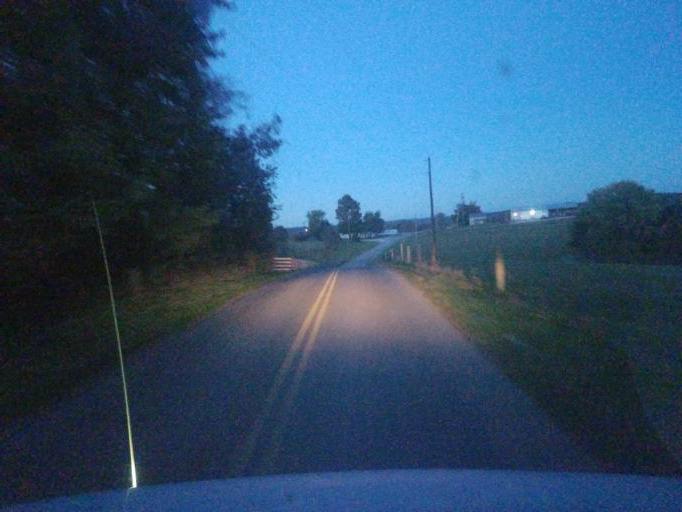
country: US
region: Ohio
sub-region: Perry County
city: Somerset
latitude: 39.8726
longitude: -82.2244
